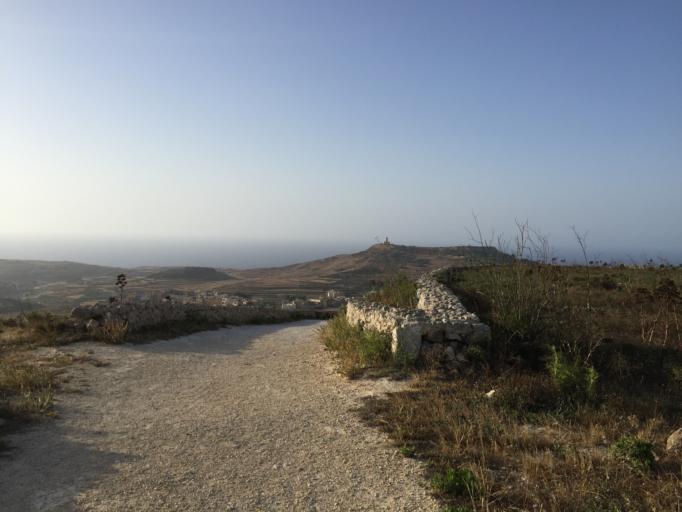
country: MT
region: L-Gharb
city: Gharb
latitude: 36.0592
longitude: 14.2190
